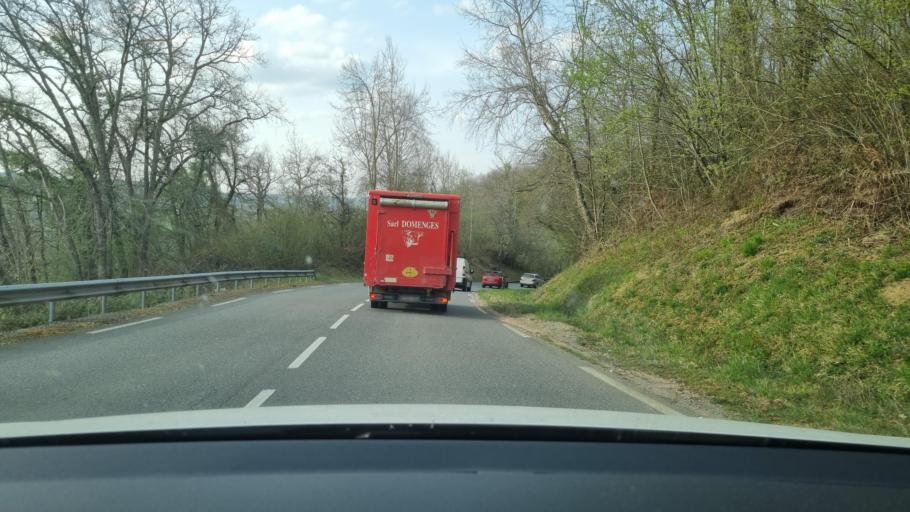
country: FR
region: Aquitaine
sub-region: Departement des Pyrenees-Atlantiques
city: Soumoulou
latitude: 43.3744
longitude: -0.1076
